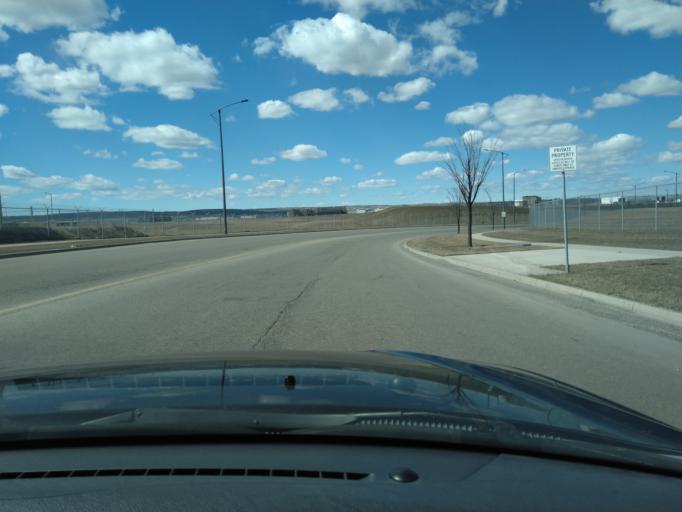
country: CA
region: Alberta
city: Calgary
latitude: 51.1376
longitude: -114.0138
